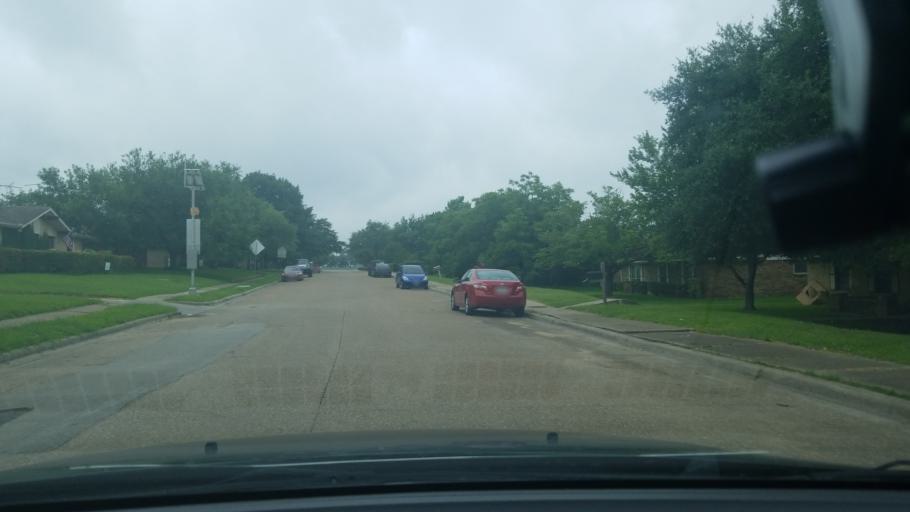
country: US
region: Texas
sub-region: Dallas County
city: Mesquite
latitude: 32.7831
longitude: -96.6389
